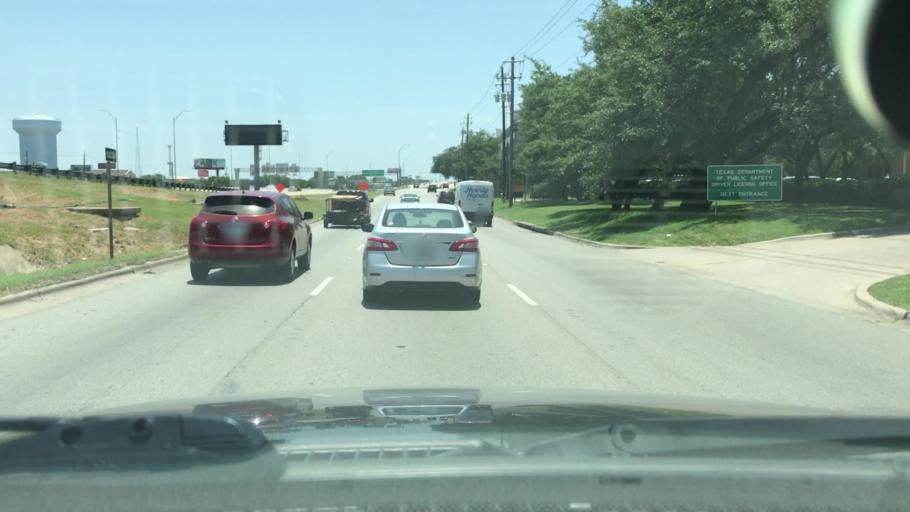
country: US
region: Texas
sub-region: Williamson County
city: Anderson Mill
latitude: 30.4587
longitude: -97.7936
